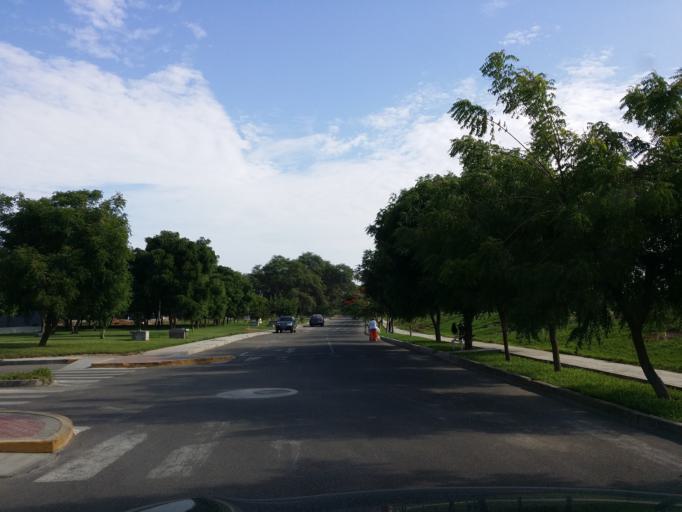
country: PE
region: Piura
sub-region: Provincia de Piura
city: Piura
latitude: -5.1749
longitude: -80.6238
